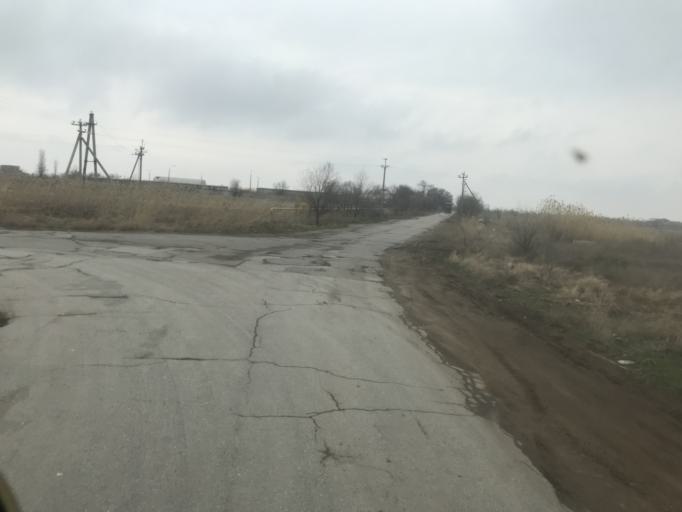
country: RU
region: Volgograd
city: Svetlyy Yar
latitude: 48.5292
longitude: 44.6098
